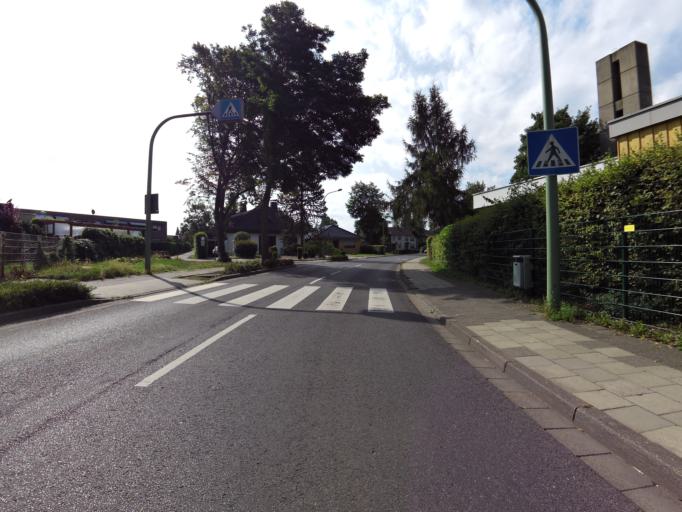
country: DE
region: North Rhine-Westphalia
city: Baesweiler
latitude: 50.9236
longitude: 6.2105
